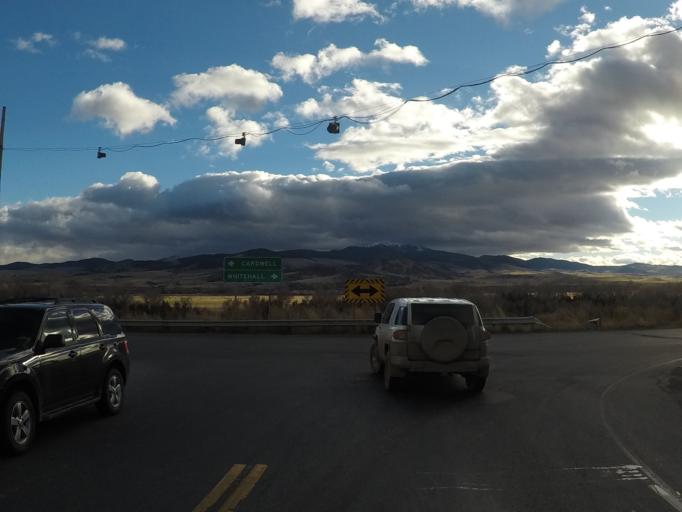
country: US
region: Montana
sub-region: Jefferson County
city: Whitehall
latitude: 45.8740
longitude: -111.9783
